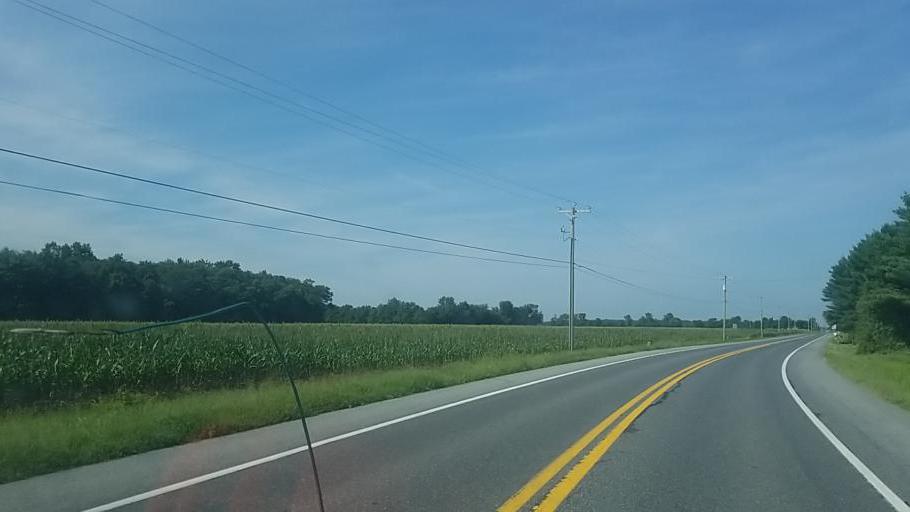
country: US
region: Delaware
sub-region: Sussex County
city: Millsboro
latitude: 38.5377
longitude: -75.2654
